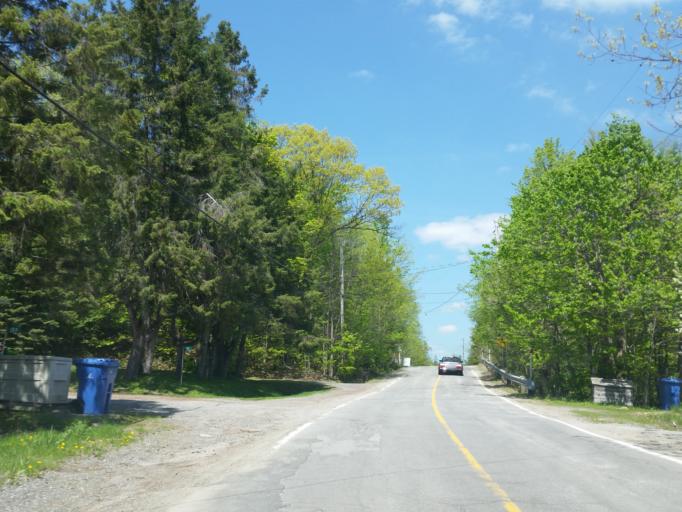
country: CA
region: Quebec
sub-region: Outaouais
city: Wakefield
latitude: 45.5923
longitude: -75.8737
